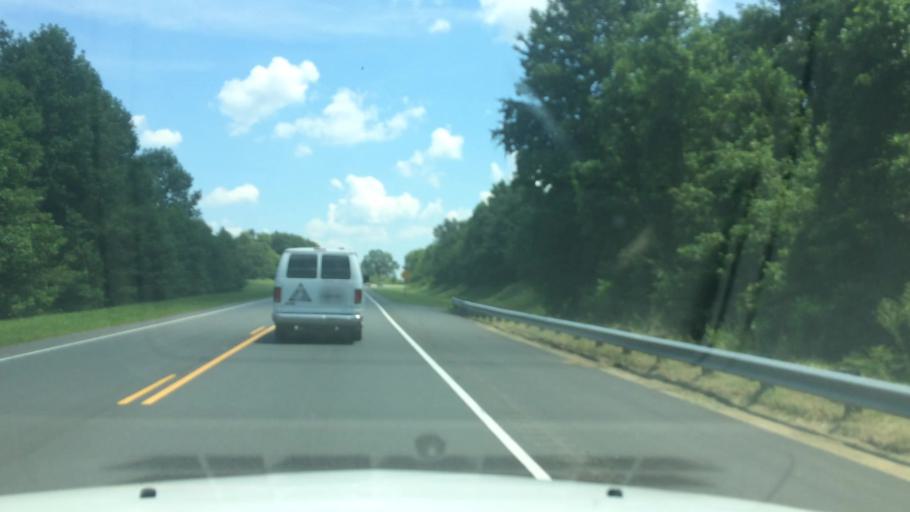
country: US
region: North Carolina
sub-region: Iredell County
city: Statesville
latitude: 35.8026
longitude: -80.9481
